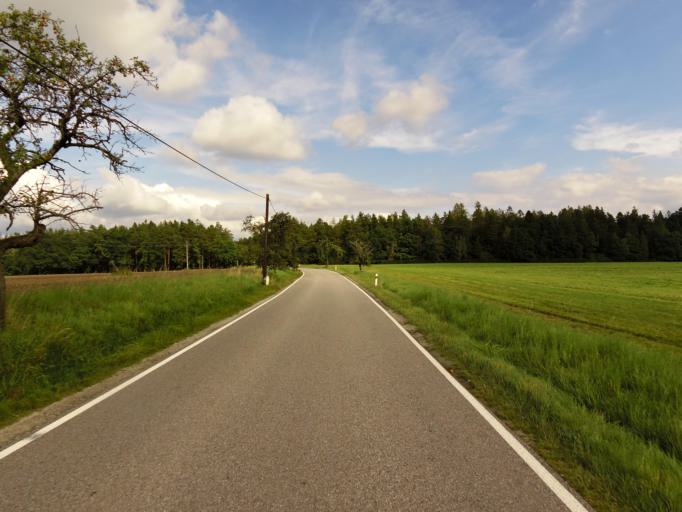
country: CZ
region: Jihocesky
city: Suchdol nad Luznici
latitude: 48.8866
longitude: 14.8229
